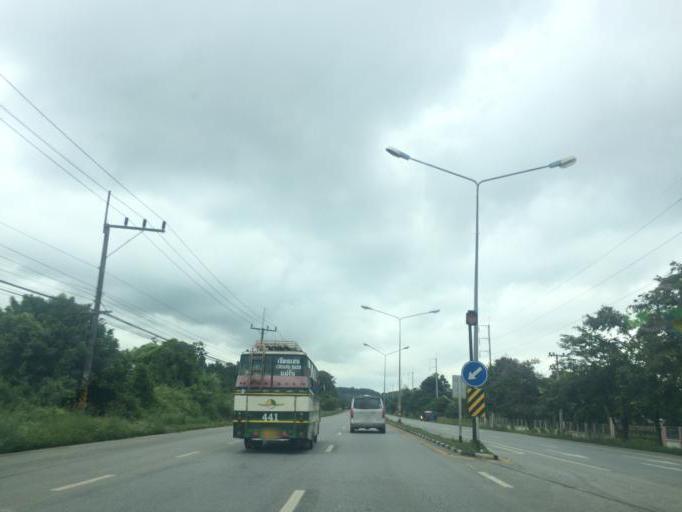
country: TH
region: Chiang Rai
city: Mae Chan
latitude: 20.0998
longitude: 99.8742
